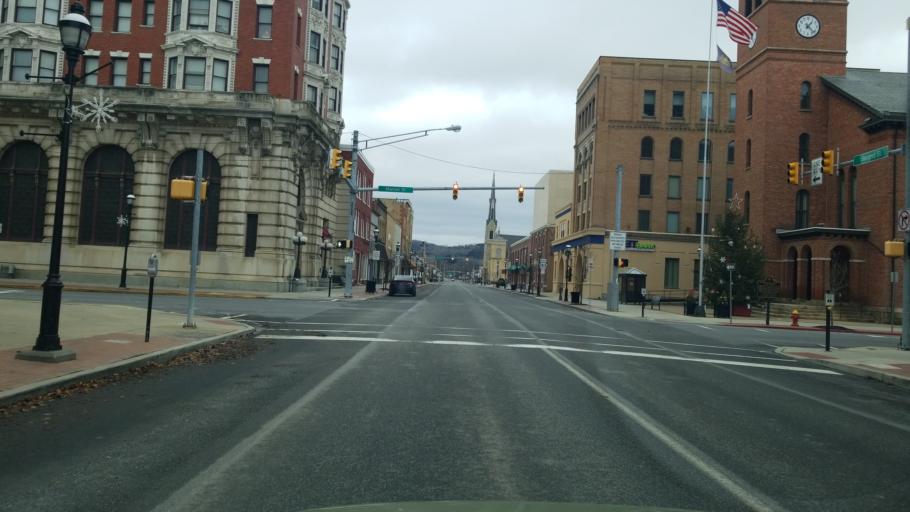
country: US
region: Pennsylvania
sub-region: Clearfield County
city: Clearfield
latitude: 41.0218
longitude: -78.4381
